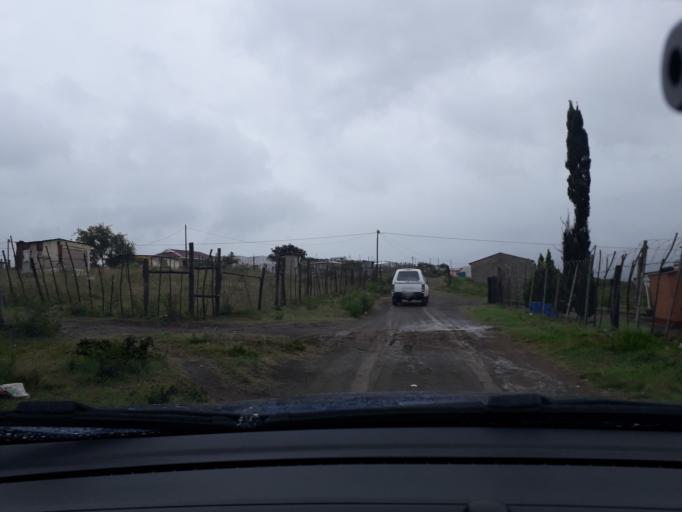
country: ZA
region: Eastern Cape
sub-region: Buffalo City Metropolitan Municipality
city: Bhisho
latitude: -32.8077
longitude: 27.3658
